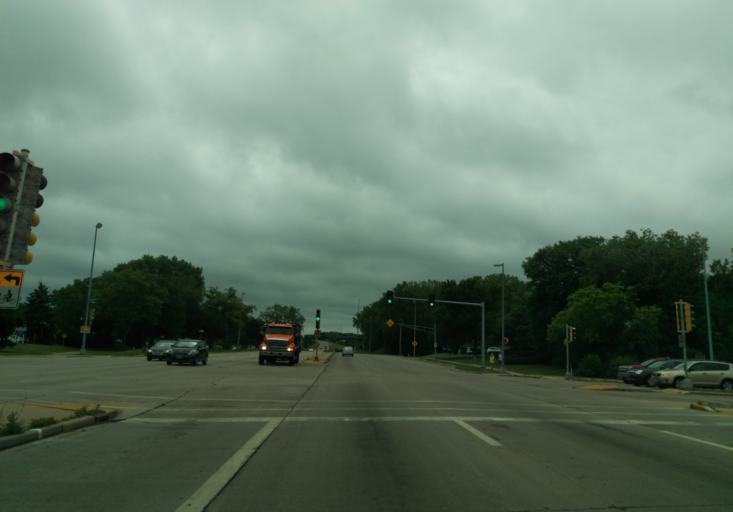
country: US
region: Wisconsin
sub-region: Dane County
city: Madison
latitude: 43.0469
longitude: -89.3746
